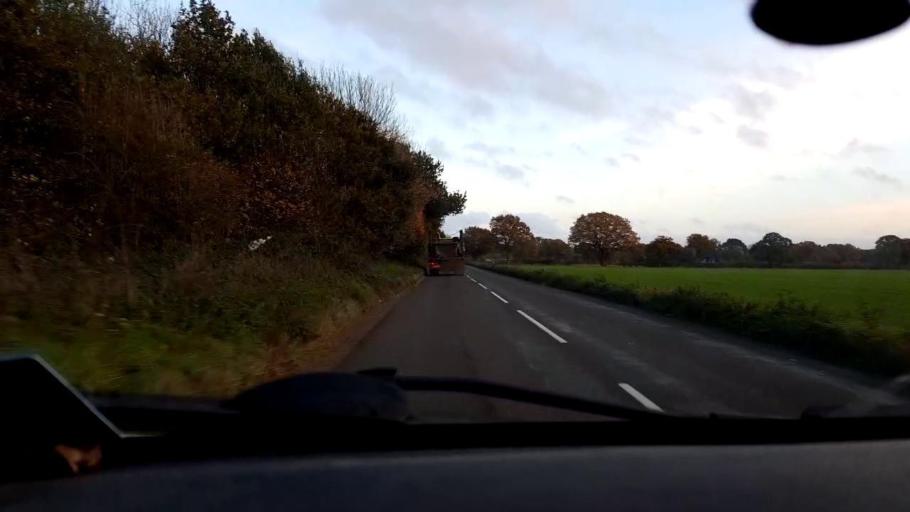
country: GB
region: England
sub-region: Norfolk
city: Mattishall
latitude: 52.6916
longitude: 1.0981
